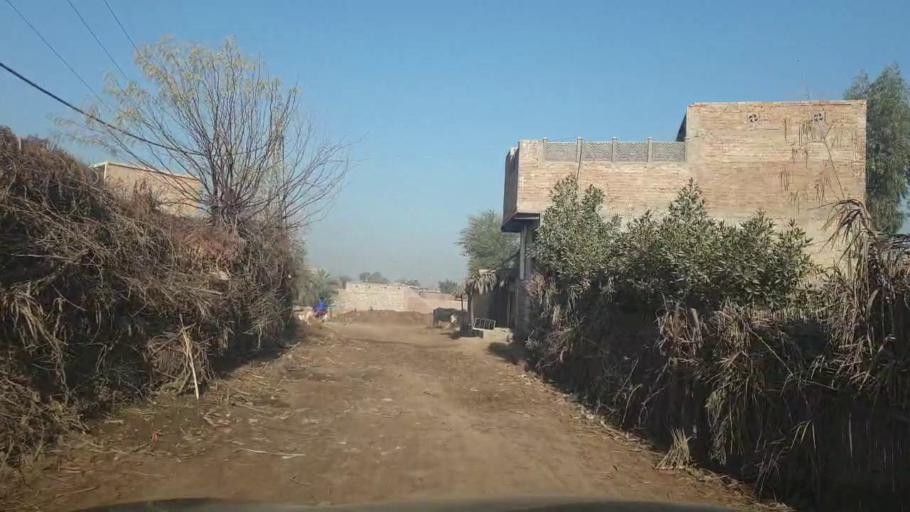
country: PK
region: Sindh
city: Mirpur Mathelo
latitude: 28.0787
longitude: 69.4687
